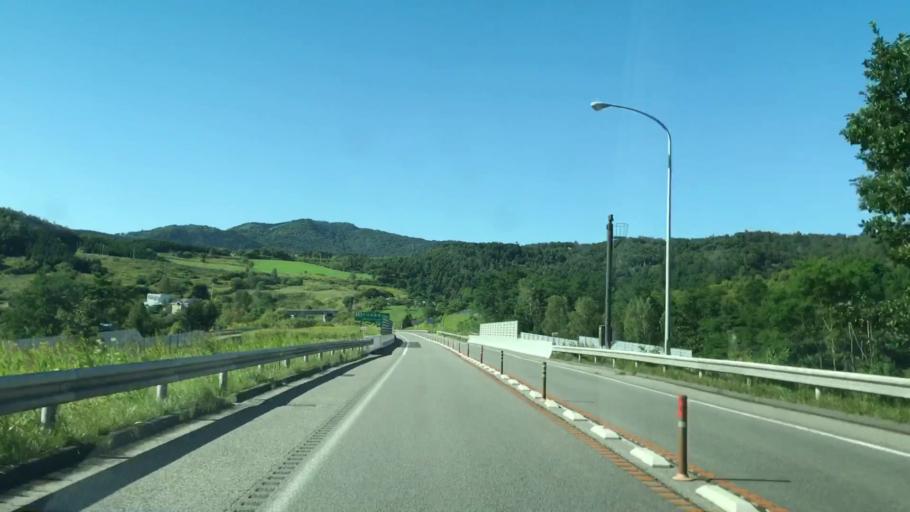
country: JP
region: Hokkaido
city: Date
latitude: 42.5472
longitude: 140.7921
